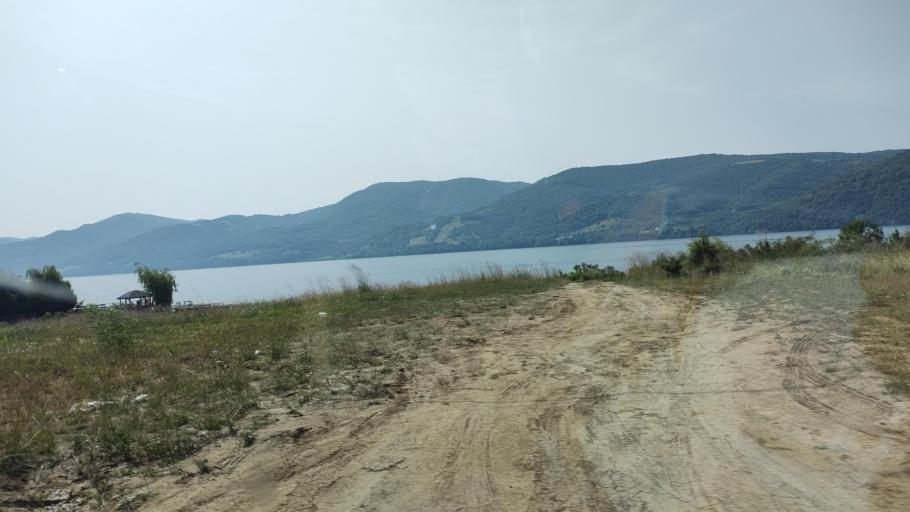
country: RO
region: Mehedinti
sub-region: Comuna Eselnita
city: Eselnita
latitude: 44.6824
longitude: 22.3408
